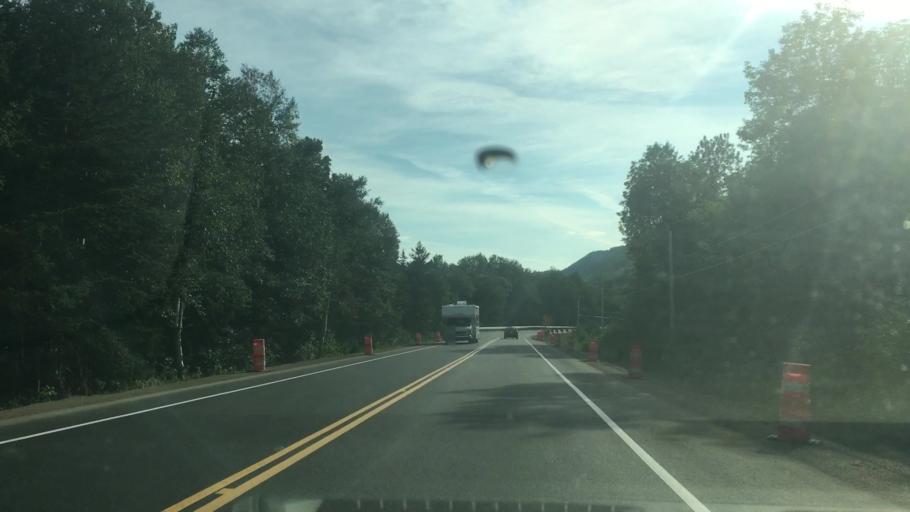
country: CA
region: Nova Scotia
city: Sydney Mines
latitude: 46.8290
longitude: -60.6168
